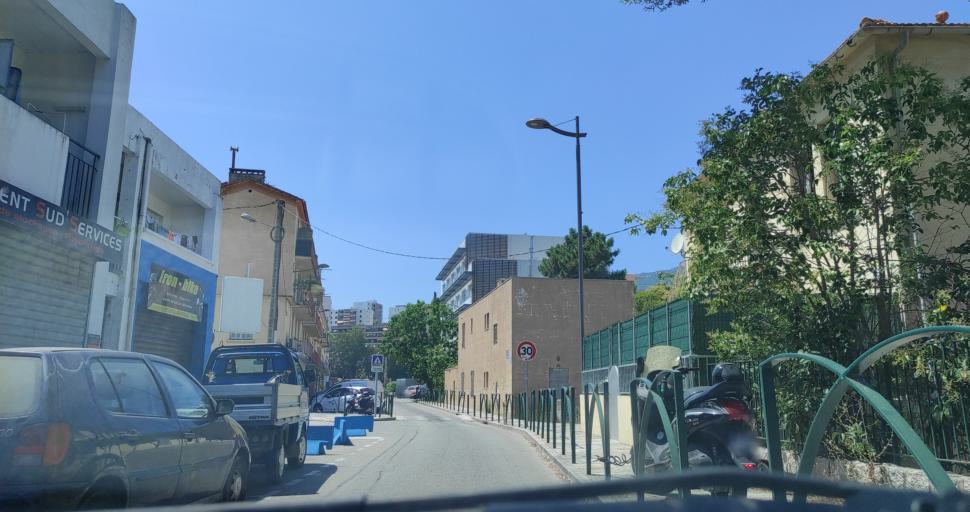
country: FR
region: Corsica
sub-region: Departement de la Corse-du-Sud
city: Ajaccio
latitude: 41.9344
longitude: 8.7400
